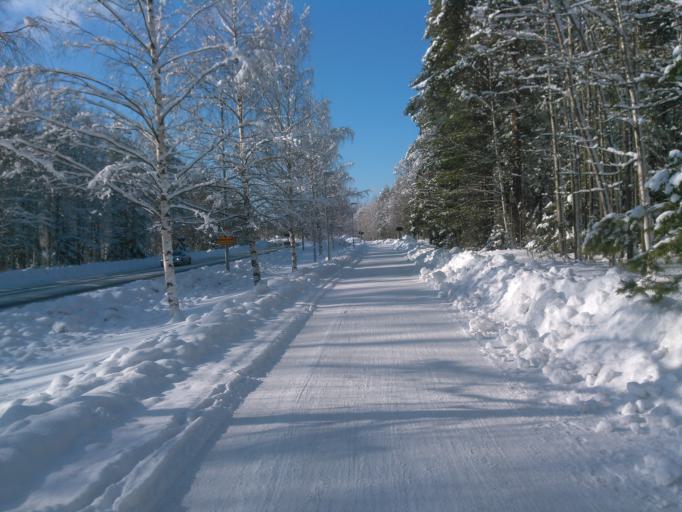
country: SE
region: Vaesterbotten
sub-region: Umea Kommun
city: Umea
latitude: 63.8142
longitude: 20.3215
